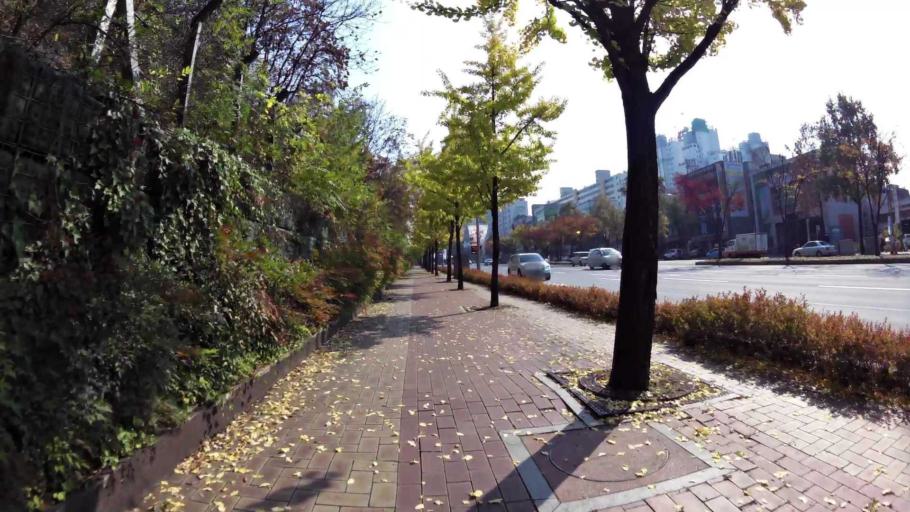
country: KR
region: Daegu
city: Daegu
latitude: 35.8561
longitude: 128.6521
